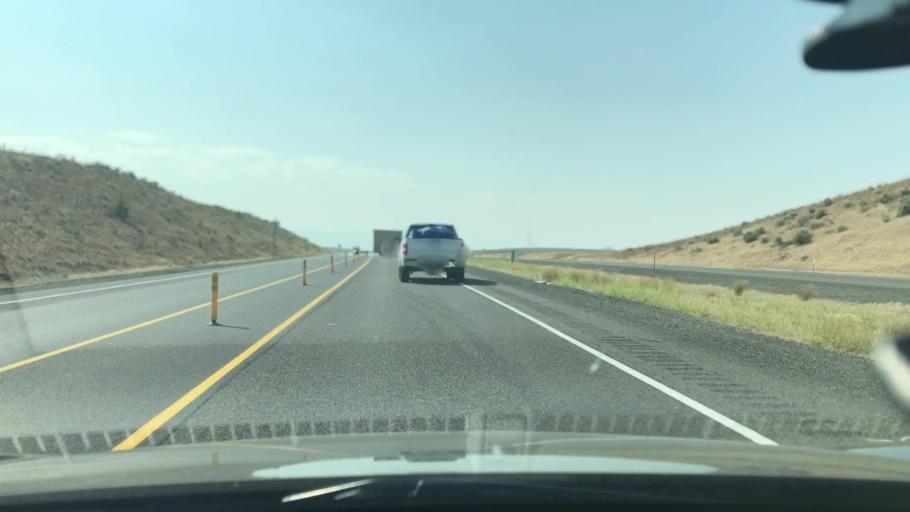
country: US
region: Oregon
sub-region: Baker County
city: Baker City
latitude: 44.6844
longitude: -117.6653
